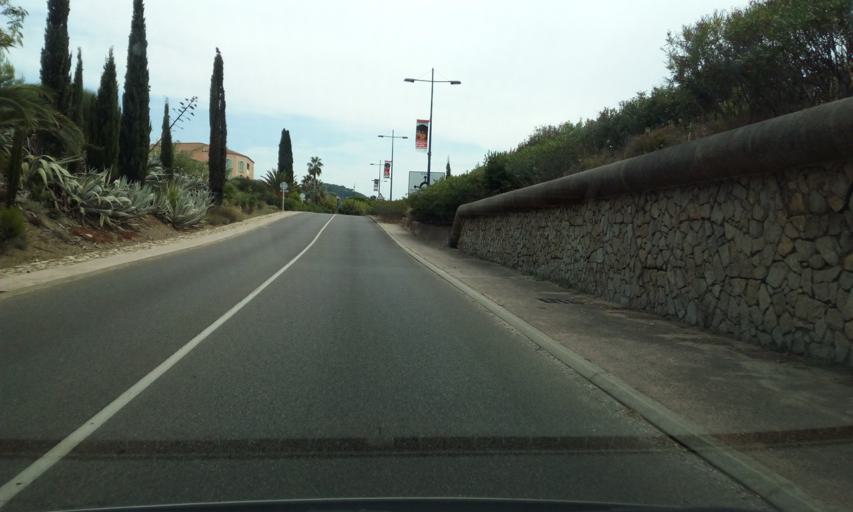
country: FR
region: Provence-Alpes-Cote d'Azur
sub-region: Departement du Var
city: Carqueiranne
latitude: 43.0928
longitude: 6.0742
